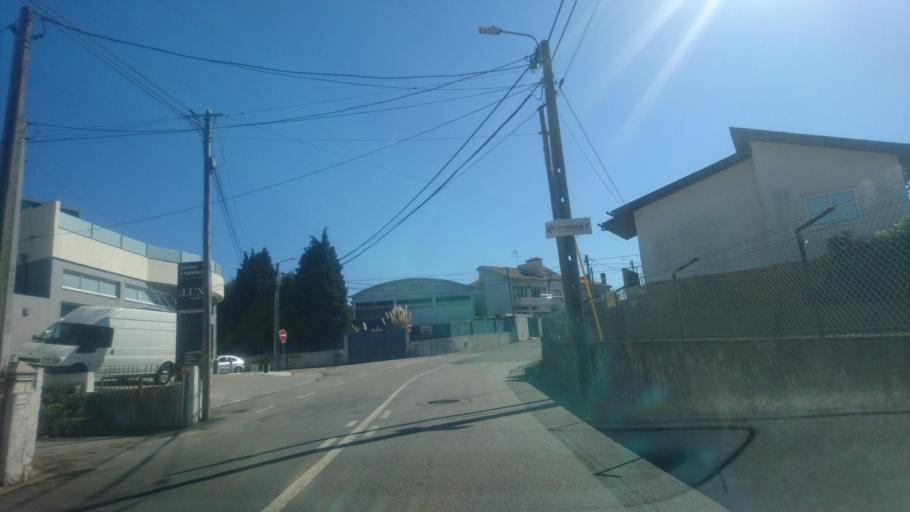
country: PT
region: Aveiro
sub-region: Santa Maria da Feira
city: Lamas
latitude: 40.9878
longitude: -8.5728
